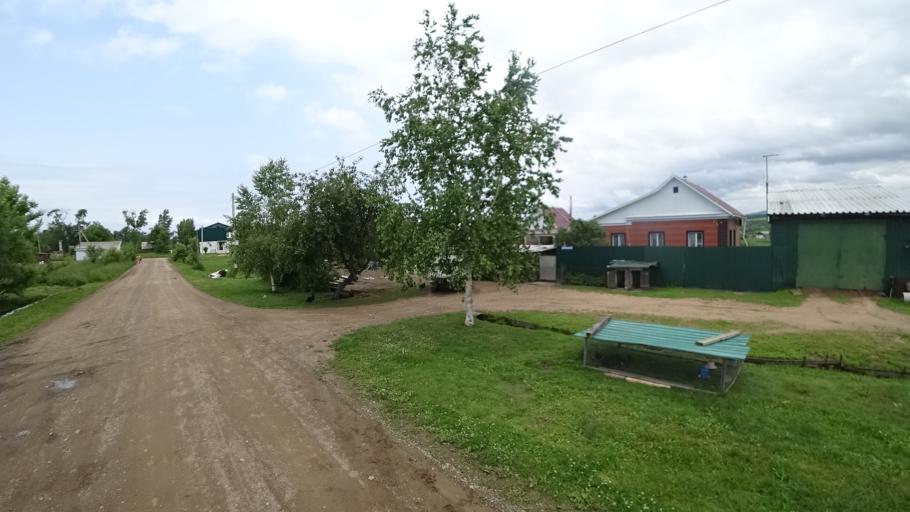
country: RU
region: Primorskiy
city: Novosysoyevka
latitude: 44.2354
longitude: 133.3644
